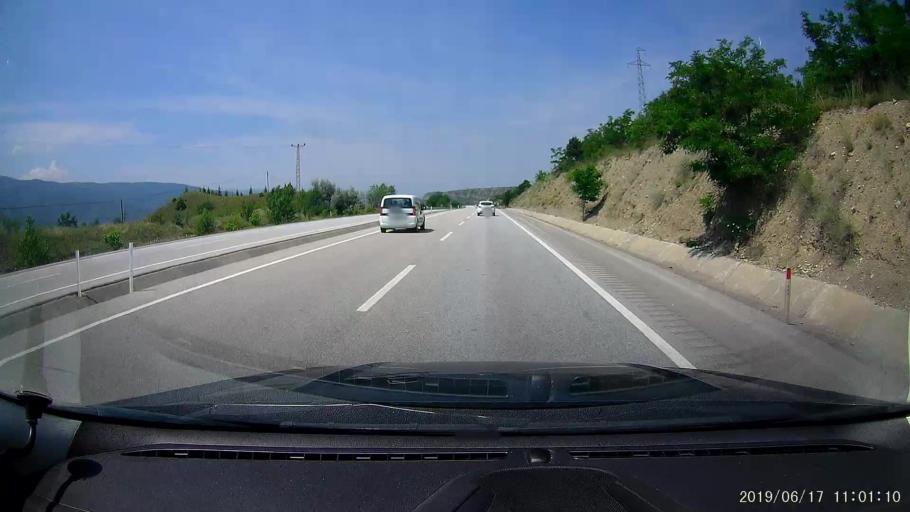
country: TR
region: Kastamonu
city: Tosya
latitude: 41.0290
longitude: 34.1619
